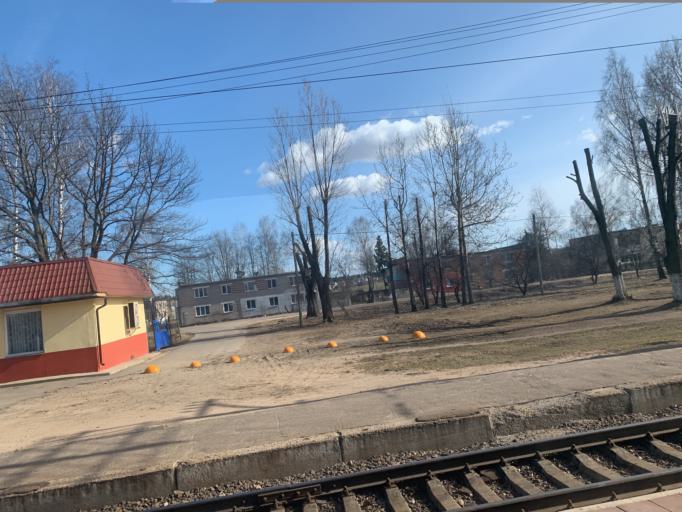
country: BY
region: Minsk
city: Shchomyslitsa
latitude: 53.8161
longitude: 27.4543
